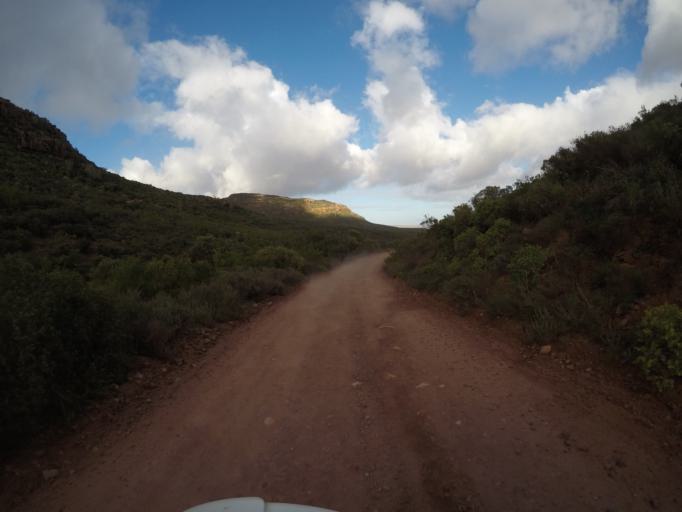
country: ZA
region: Western Cape
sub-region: West Coast District Municipality
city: Clanwilliam
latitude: -32.3407
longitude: 18.7783
